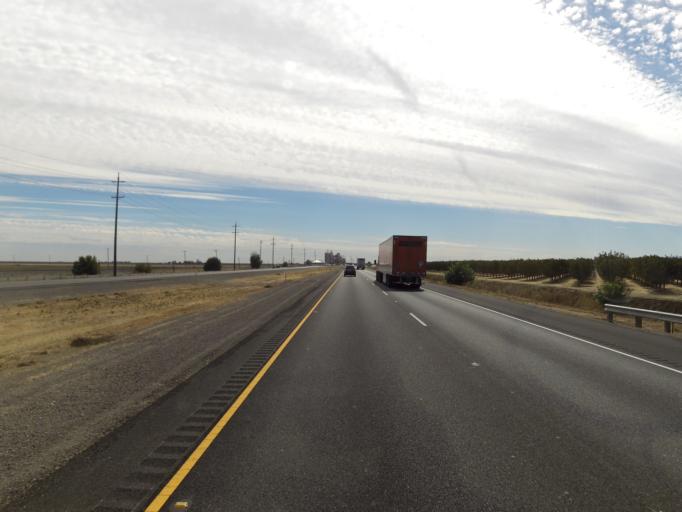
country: US
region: California
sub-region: Colusa County
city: Arbuckle
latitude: 39.0775
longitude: -122.0972
